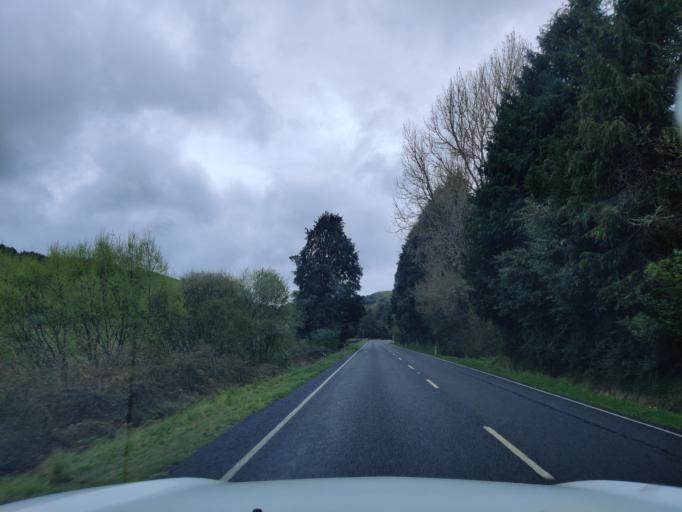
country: NZ
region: Waikato
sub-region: Otorohanga District
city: Otorohanga
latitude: -38.5585
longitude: 175.1956
